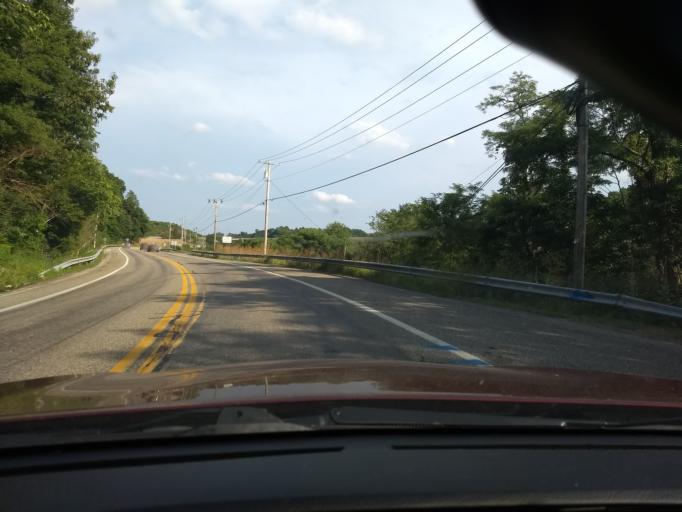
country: US
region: Pennsylvania
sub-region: Allegheny County
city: Tarentum
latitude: 40.6172
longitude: -79.7625
